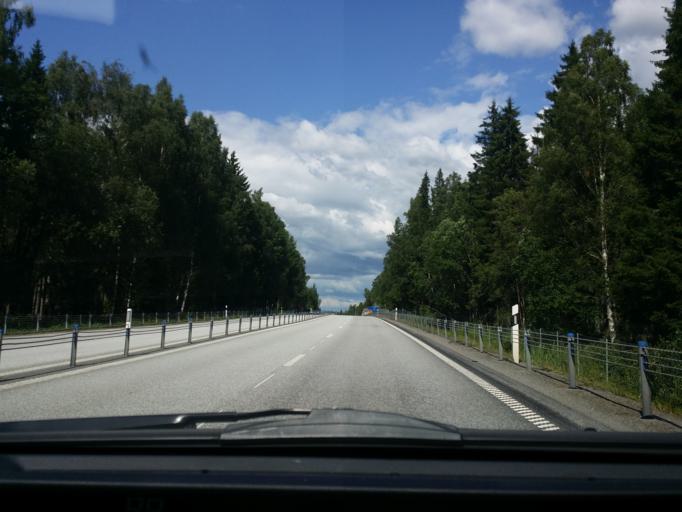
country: SE
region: OErebro
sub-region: Orebro Kommun
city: Hovsta
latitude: 59.3791
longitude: 15.2185
